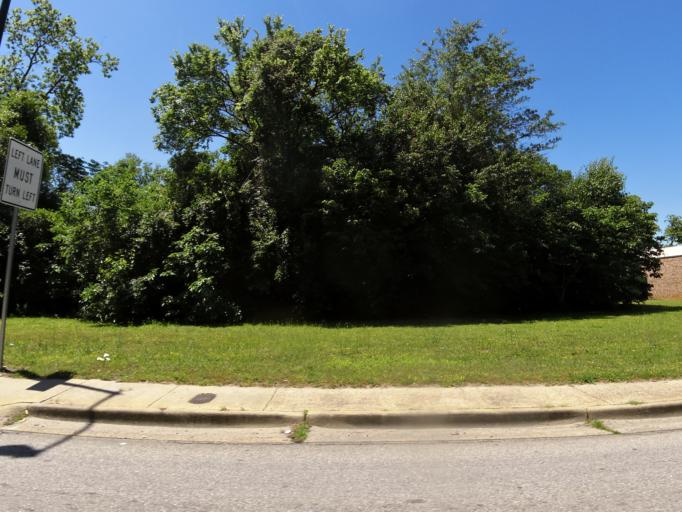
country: US
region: Georgia
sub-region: Richmond County
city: Augusta
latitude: 33.4695
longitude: -81.9725
